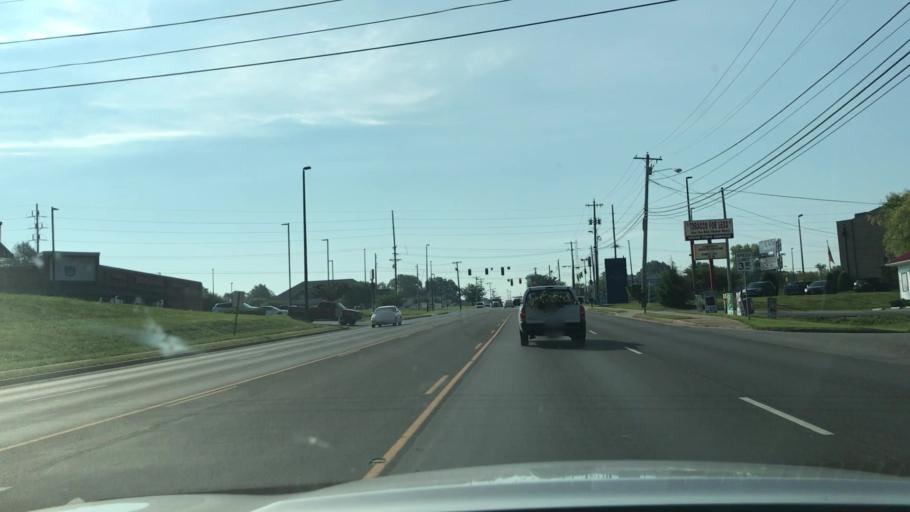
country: US
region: Kentucky
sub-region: Barren County
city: Glasgow
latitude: 37.0030
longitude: -85.9281
